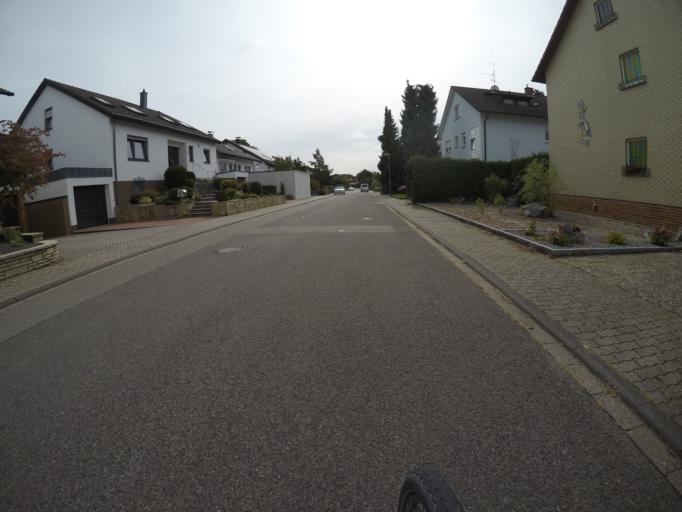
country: DE
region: Baden-Wuerttemberg
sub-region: Karlsruhe Region
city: Ubstadt-Weiher
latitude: 49.1600
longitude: 8.6369
